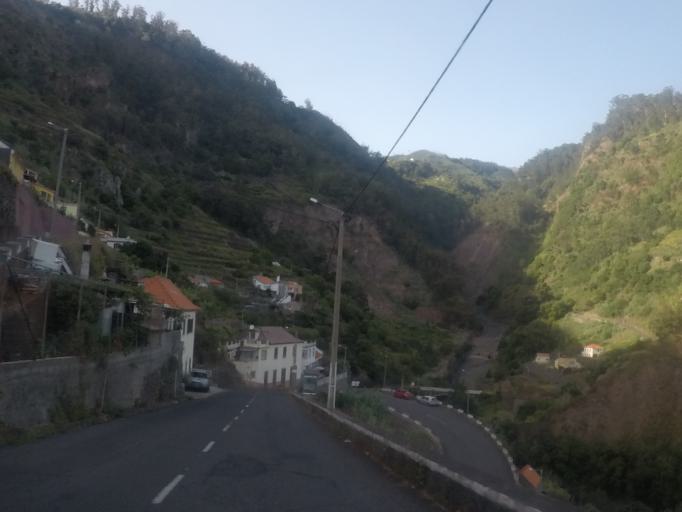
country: PT
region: Madeira
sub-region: Calheta
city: Arco da Calheta
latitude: 32.7115
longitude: -17.1353
